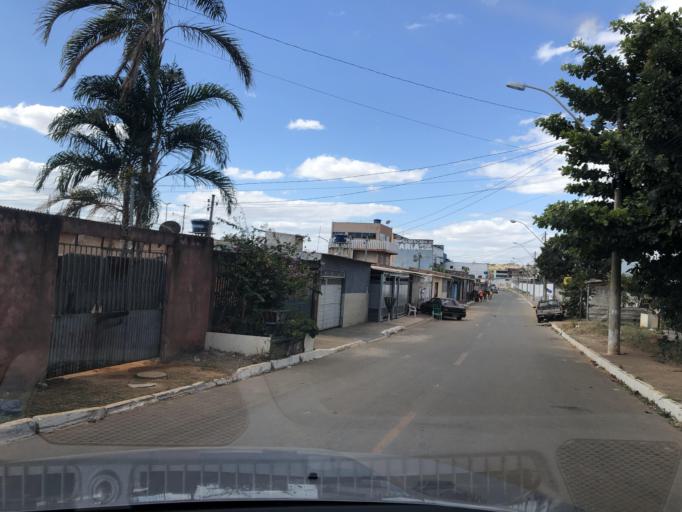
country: BR
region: Federal District
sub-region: Brasilia
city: Brasilia
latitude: -15.8887
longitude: -48.1498
